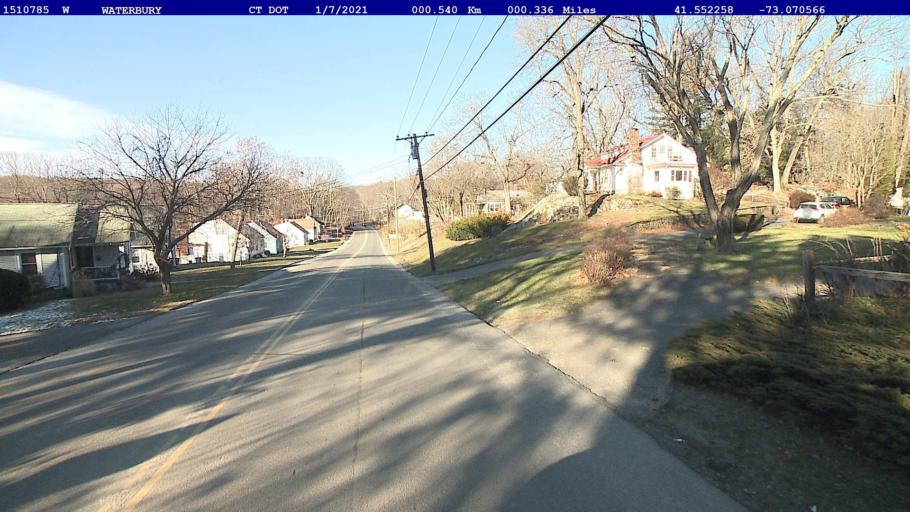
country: US
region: Connecticut
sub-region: New Haven County
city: Waterbury
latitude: 41.5523
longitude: -73.0706
